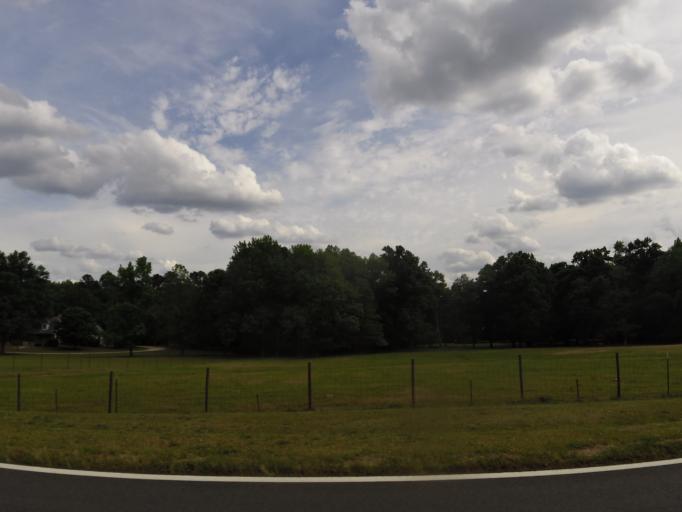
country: US
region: Georgia
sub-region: McDuffie County
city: Thomson
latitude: 33.5222
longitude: -82.4540
